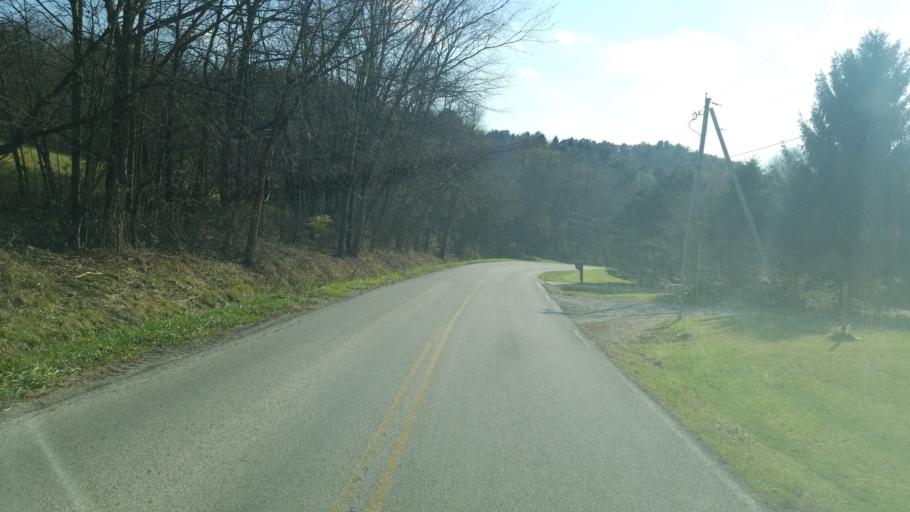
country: US
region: Ohio
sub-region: Sandusky County
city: Bellville
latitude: 40.6212
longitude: -82.4444
